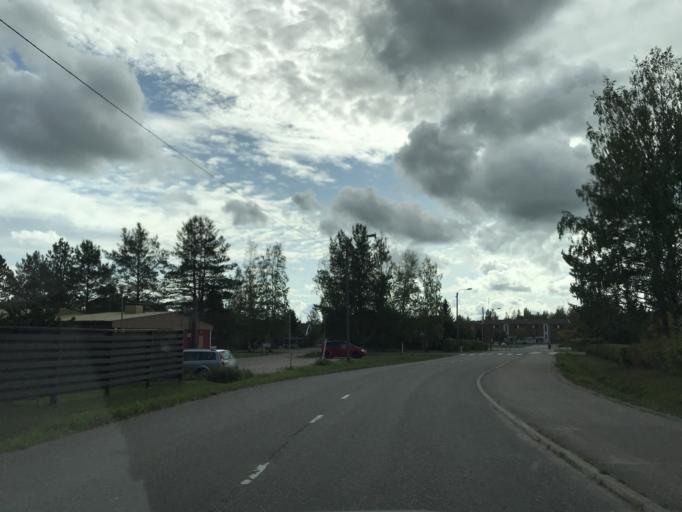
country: FI
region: Paijanne Tavastia
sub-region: Lahti
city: Orimattila
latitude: 60.8119
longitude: 25.7255
